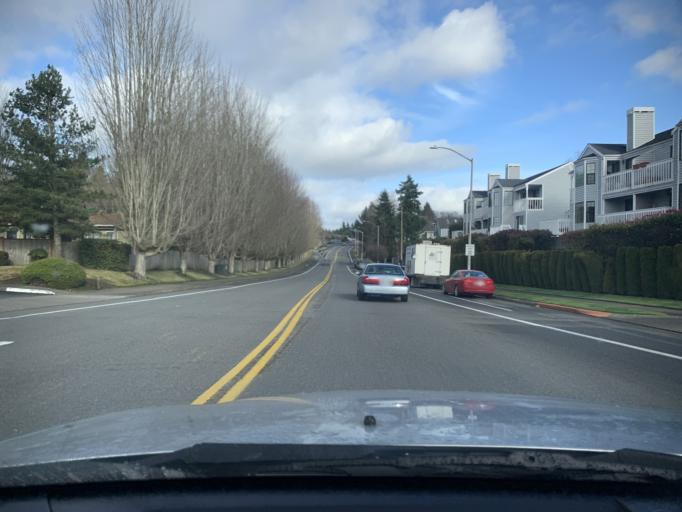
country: US
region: Washington
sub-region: Pierce County
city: Fircrest
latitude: 47.2726
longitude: -122.5238
